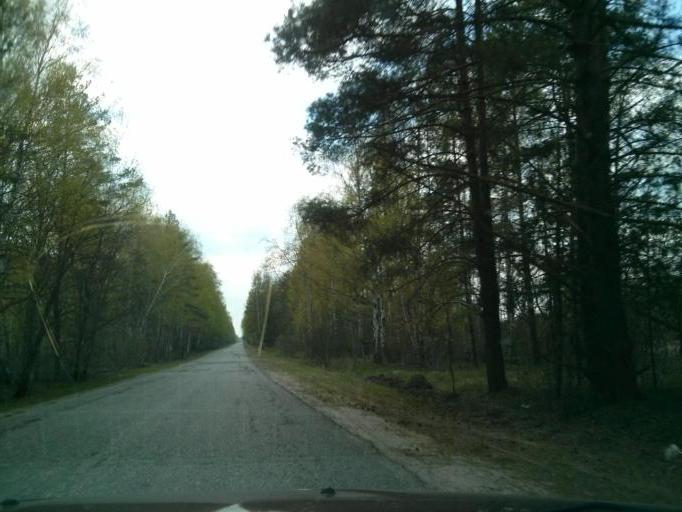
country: RU
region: Nizjnij Novgorod
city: Shimorskoye
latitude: 55.3409
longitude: 41.8500
